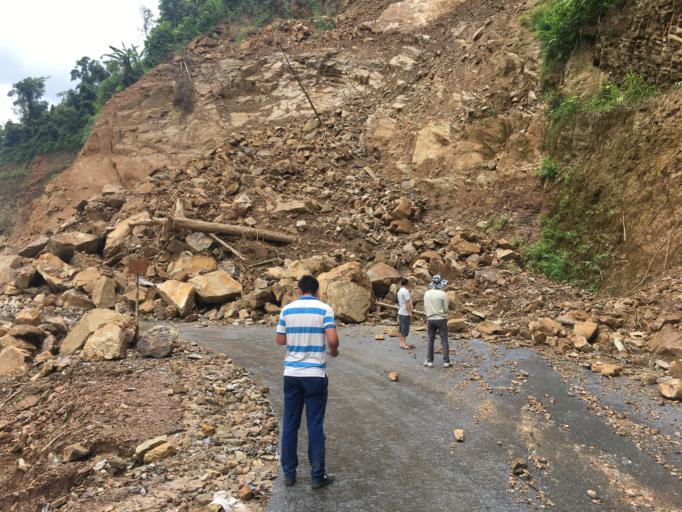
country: VN
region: Ha Giang
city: Thi Tran Tam Son
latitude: 22.9797
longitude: 105.0561
